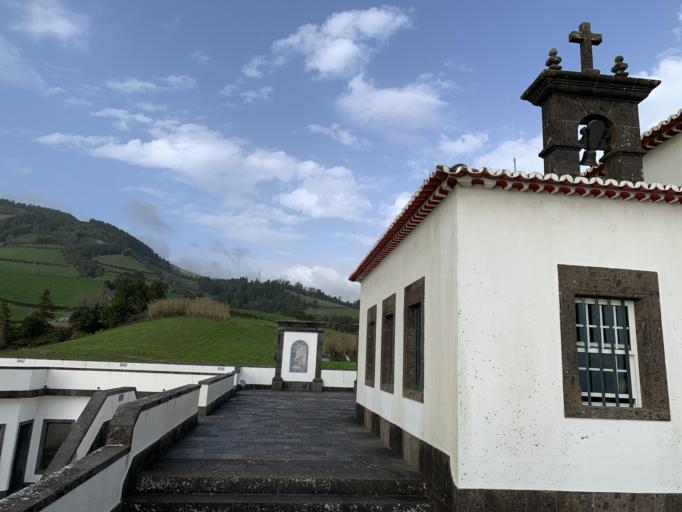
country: PT
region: Azores
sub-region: Vila Franca do Campo
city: Vila Franca do Campo
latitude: 37.7285
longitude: -25.4315
